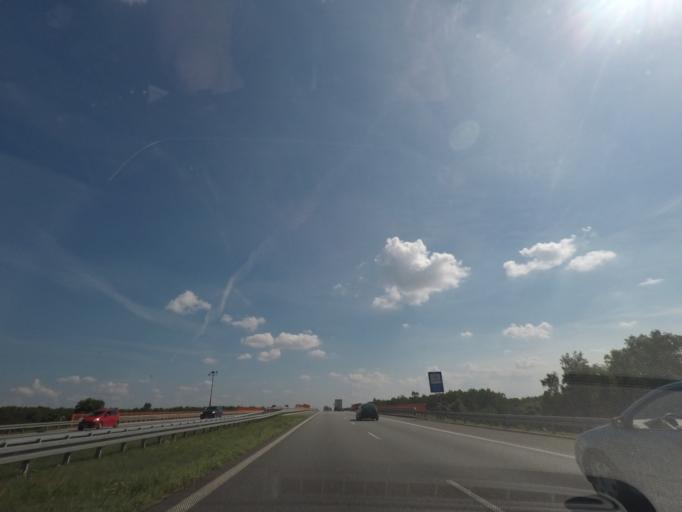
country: PL
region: Lodz Voivodeship
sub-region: Powiat lodzki wschodni
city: Andrespol
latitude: 51.7338
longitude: 19.6029
